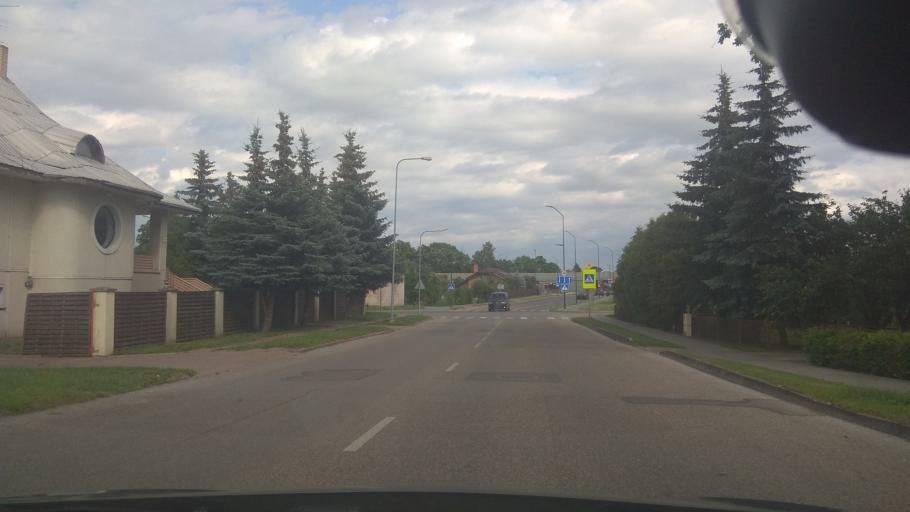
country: LT
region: Marijampoles apskritis
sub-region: Marijampole Municipality
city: Marijampole
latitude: 54.5450
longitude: 23.3524
